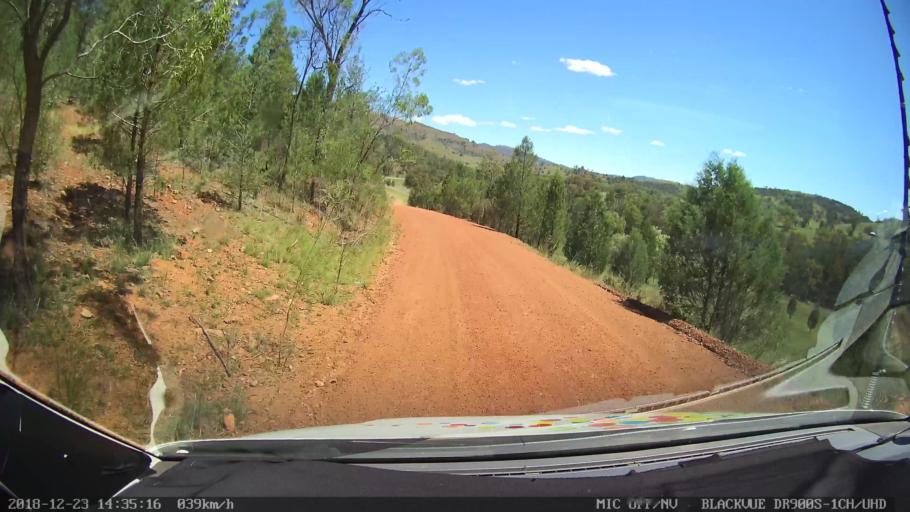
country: AU
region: New South Wales
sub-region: Tamworth Municipality
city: Manilla
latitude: -30.6091
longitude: 150.9076
